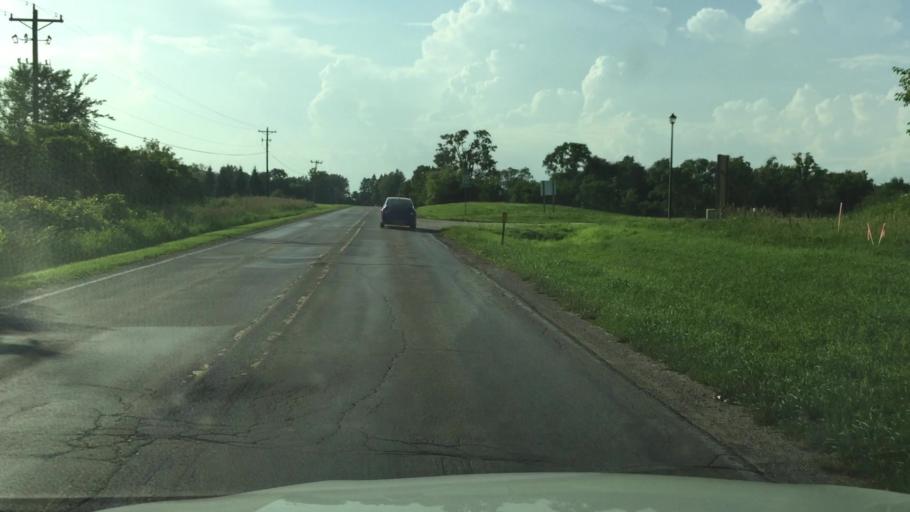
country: US
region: Iowa
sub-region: Linn County
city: Ely
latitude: 41.8372
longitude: -91.6375
